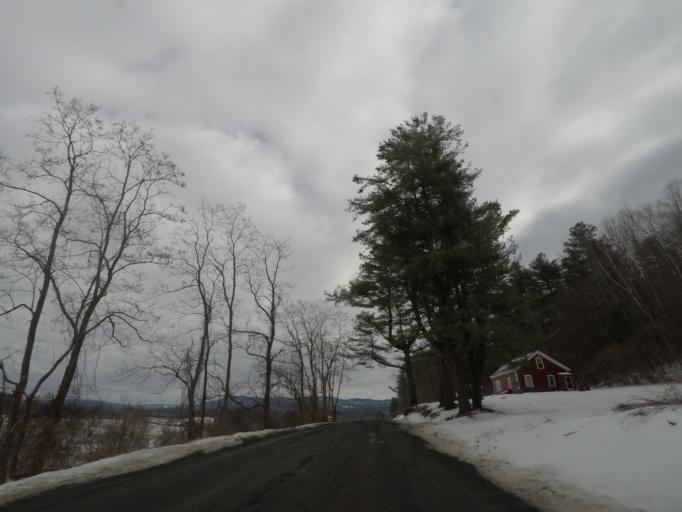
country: US
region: New York
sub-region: Rensselaer County
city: Hoosick Falls
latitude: 42.8649
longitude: -73.3665
